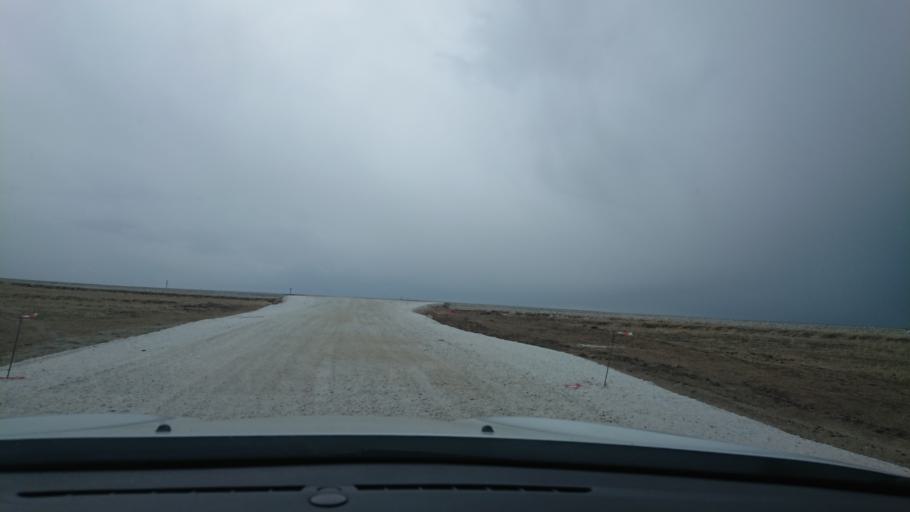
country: TR
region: Aksaray
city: Agacoren
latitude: 38.9456
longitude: 33.9131
